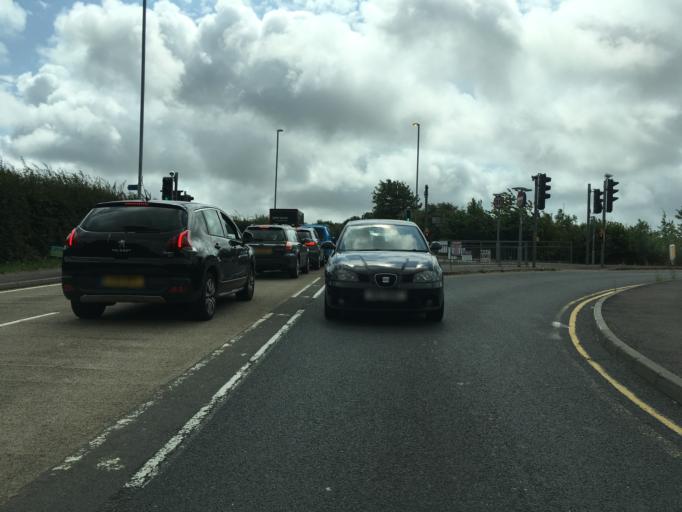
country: GB
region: England
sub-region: Brighton and Hove
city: Rottingdean
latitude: 50.8614
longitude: -0.0792
